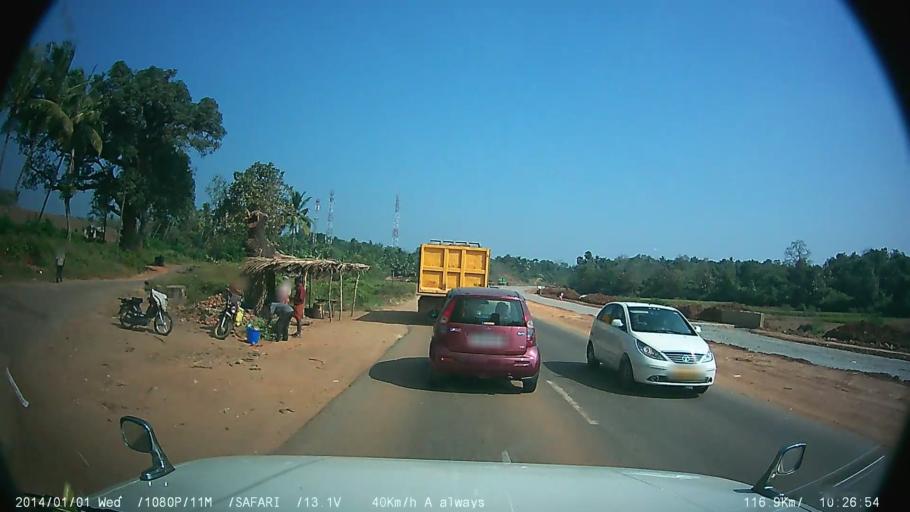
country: IN
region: Kerala
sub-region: Thrissur District
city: Chelakara
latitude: 10.6301
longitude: 76.5136
